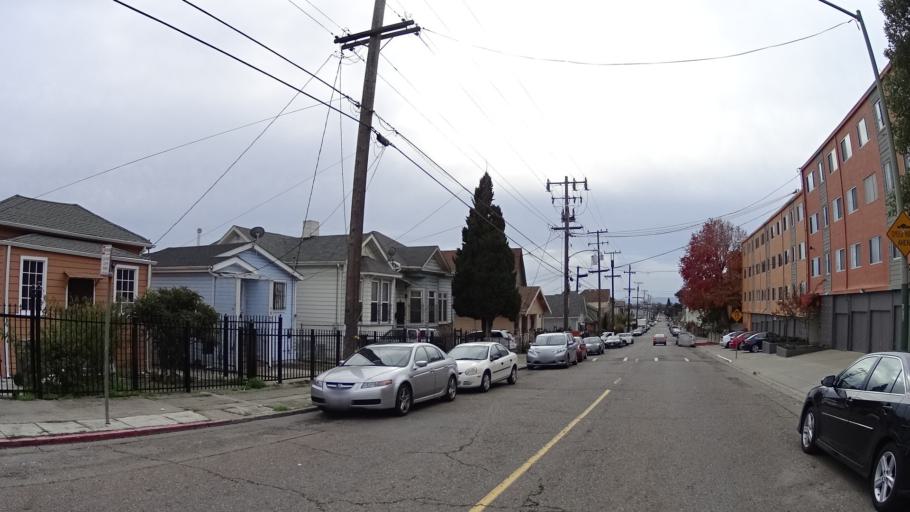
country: US
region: California
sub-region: Alameda County
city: Alameda
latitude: 37.7938
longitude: -122.2417
